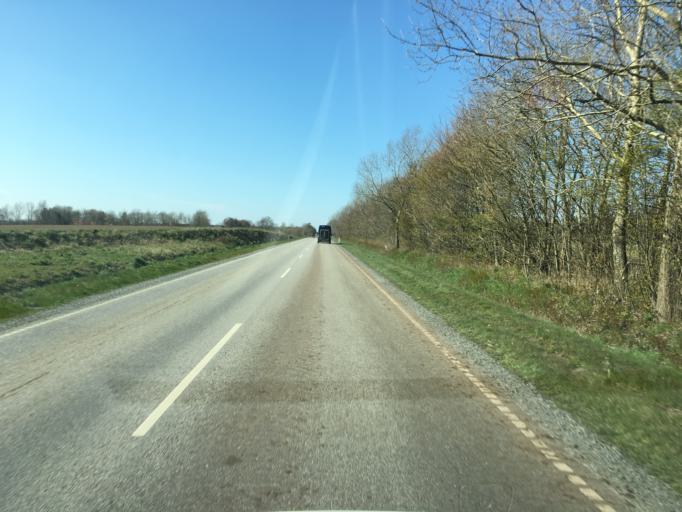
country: DK
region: South Denmark
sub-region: Aabenraa Kommune
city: Tinglev
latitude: 54.9550
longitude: 9.3381
